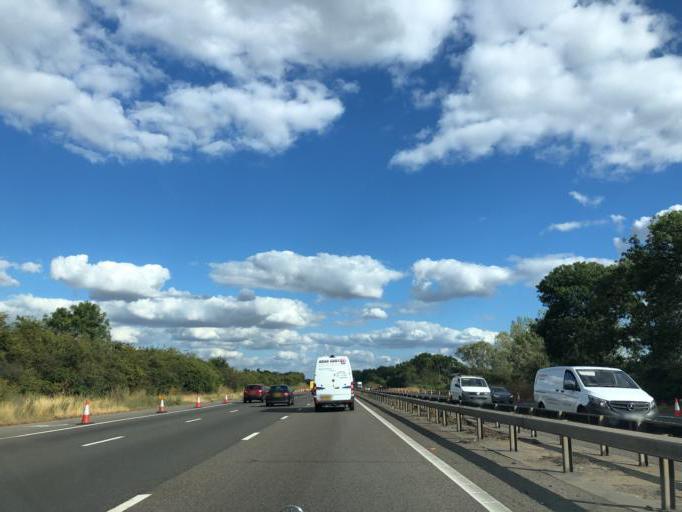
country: GB
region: England
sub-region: Milton Keynes
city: Woburn Sands
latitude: 52.0399
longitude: -0.6497
